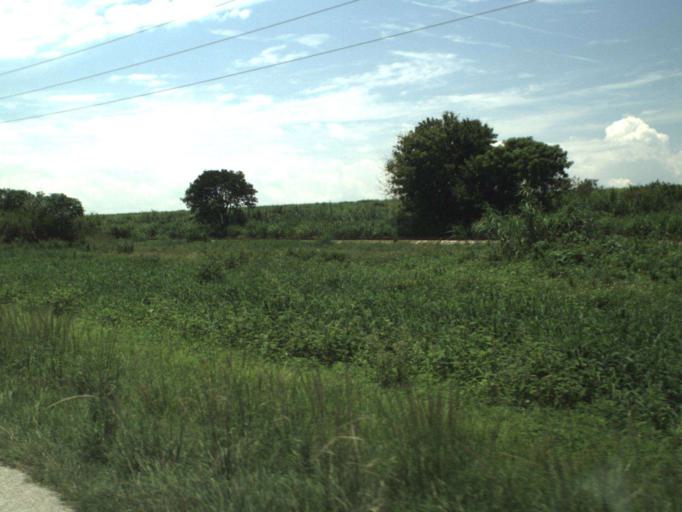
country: US
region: Florida
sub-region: Palm Beach County
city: Pahokee
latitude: 26.8834
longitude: -80.6174
